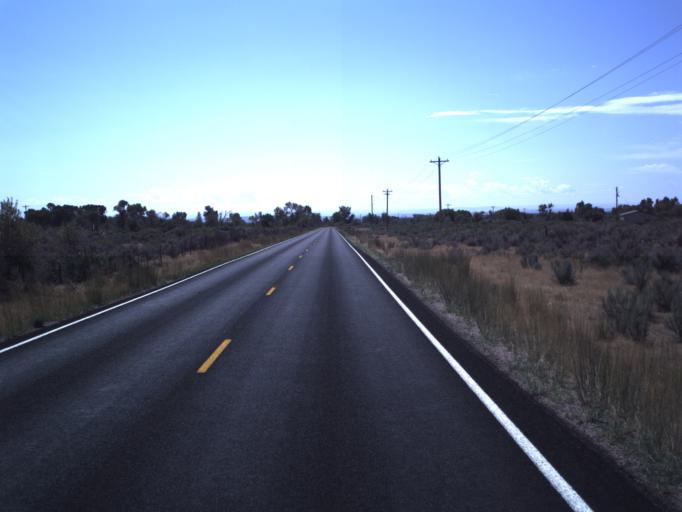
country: US
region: Utah
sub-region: Duchesne County
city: Roosevelt
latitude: 40.4168
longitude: -109.9195
